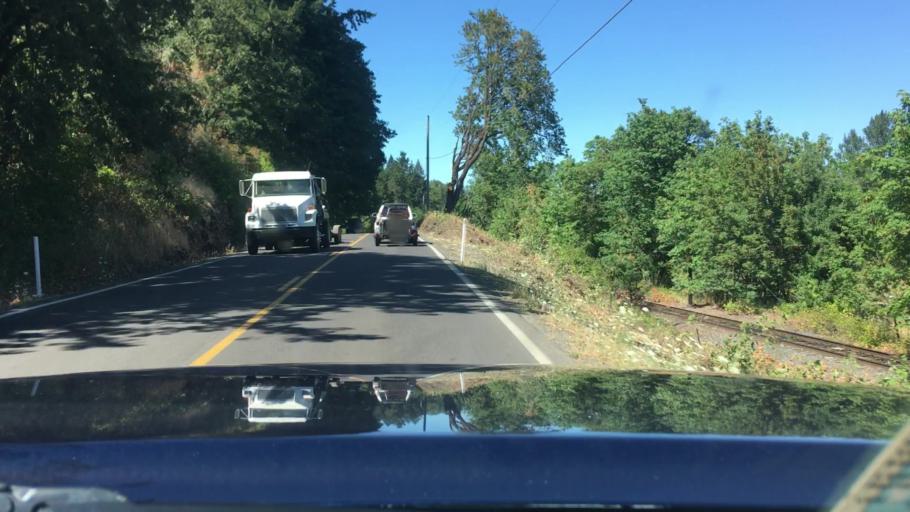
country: US
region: Oregon
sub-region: Lane County
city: Cottage Grove
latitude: 43.8177
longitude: -123.0459
